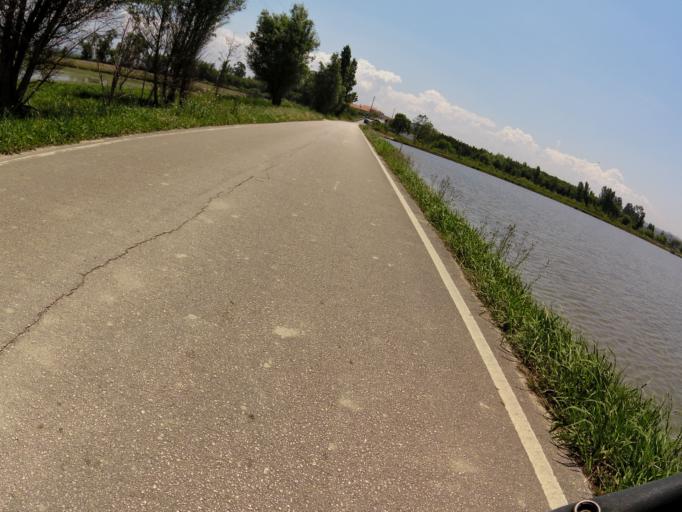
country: PT
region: Coimbra
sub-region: Montemor-O-Velho
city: Montemor-o-Velho
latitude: 40.1623
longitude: -8.7162
